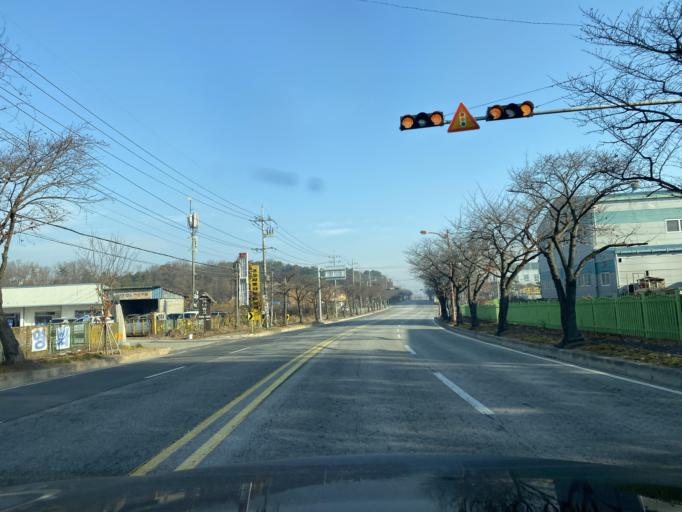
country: KR
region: Chungcheongnam-do
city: Yesan
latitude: 36.7134
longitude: 126.8415
